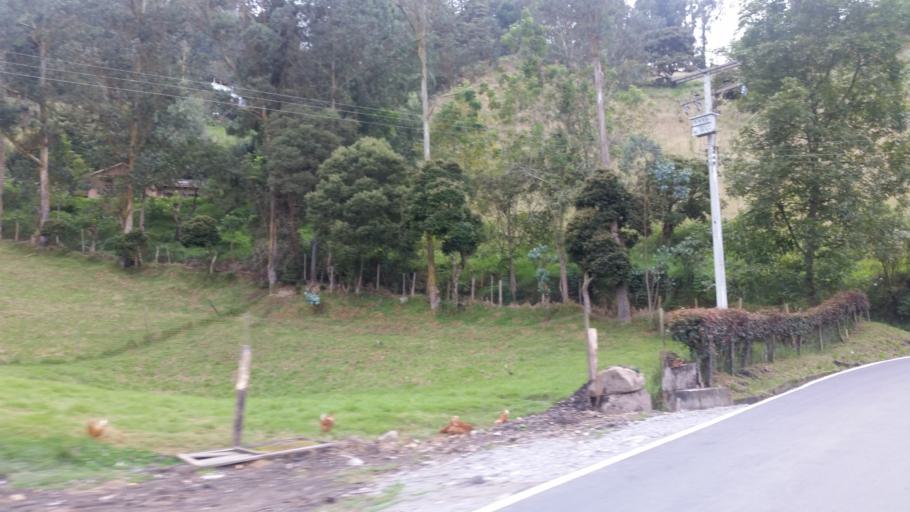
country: CO
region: Cundinamarca
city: Choachi
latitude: 4.5548
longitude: -73.9352
